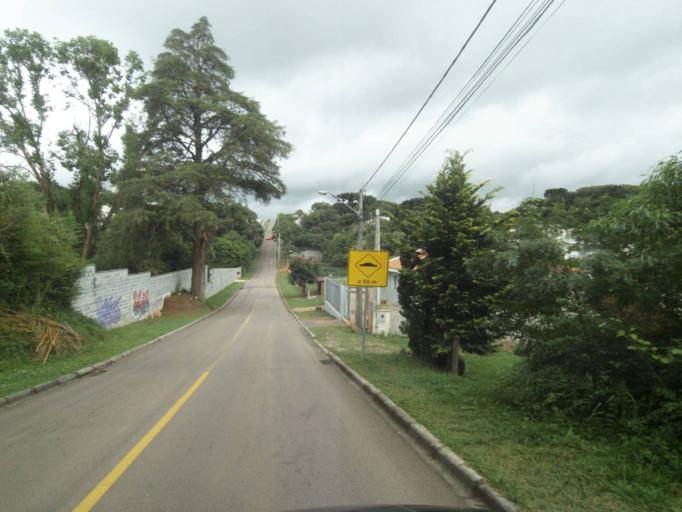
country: BR
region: Parana
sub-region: Curitiba
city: Curitiba
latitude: -25.4472
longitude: -49.3341
